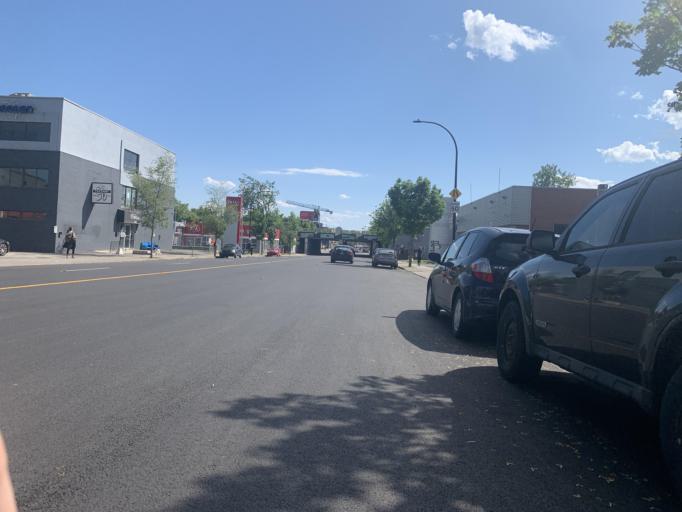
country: CA
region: Quebec
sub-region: Monteregie
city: Longueuil
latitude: 45.5410
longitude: -73.5551
